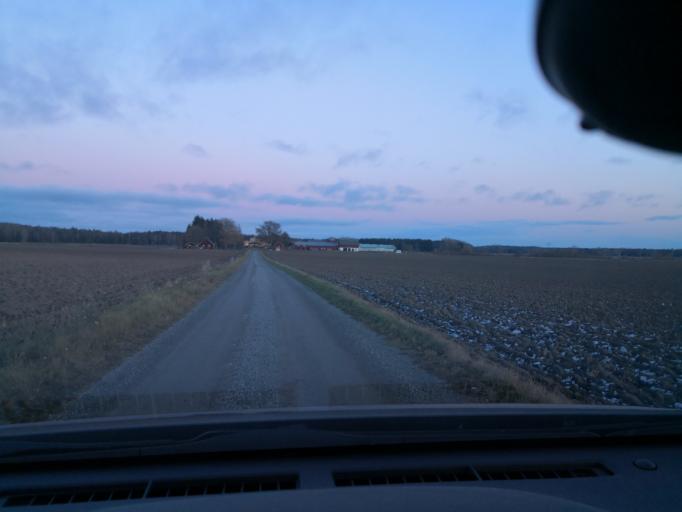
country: SE
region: Vaestmanland
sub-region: Vasteras
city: Tillberga
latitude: 59.7904
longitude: 16.6341
